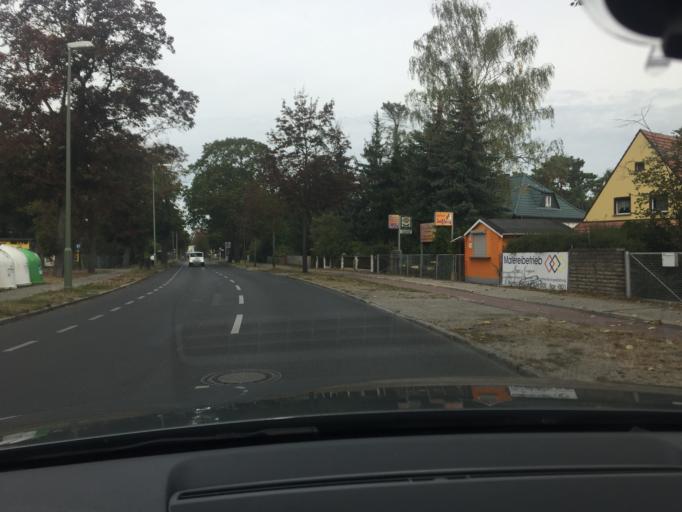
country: DE
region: Berlin
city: Rahnsdorf
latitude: 52.4384
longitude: 13.6947
